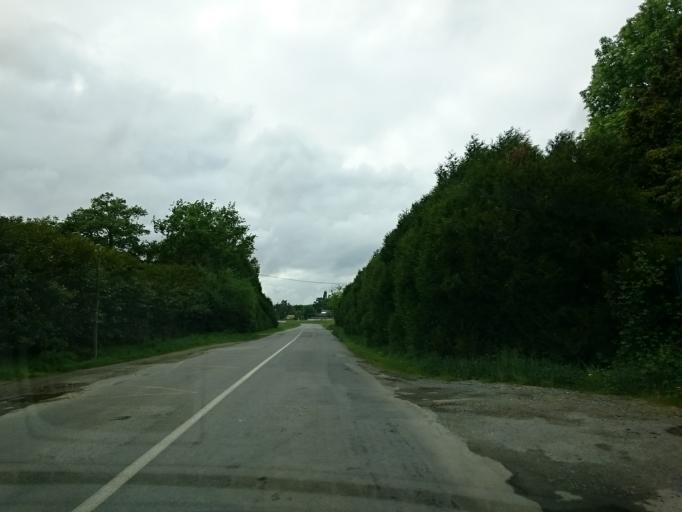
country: FR
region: Brittany
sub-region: Departement d'Ille-et-Vilaine
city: Chantepie
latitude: 48.0654
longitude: -1.6203
